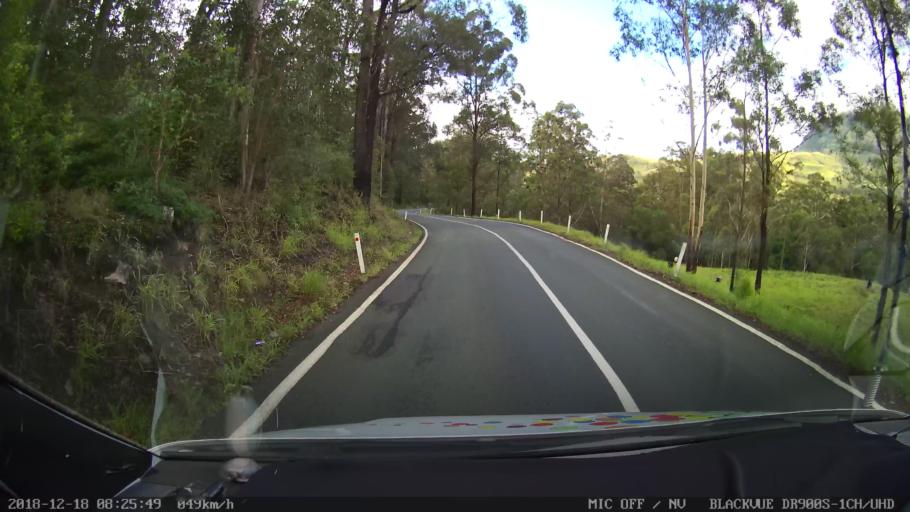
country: AU
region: New South Wales
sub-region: Kyogle
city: Kyogle
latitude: -28.3238
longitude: 152.7406
